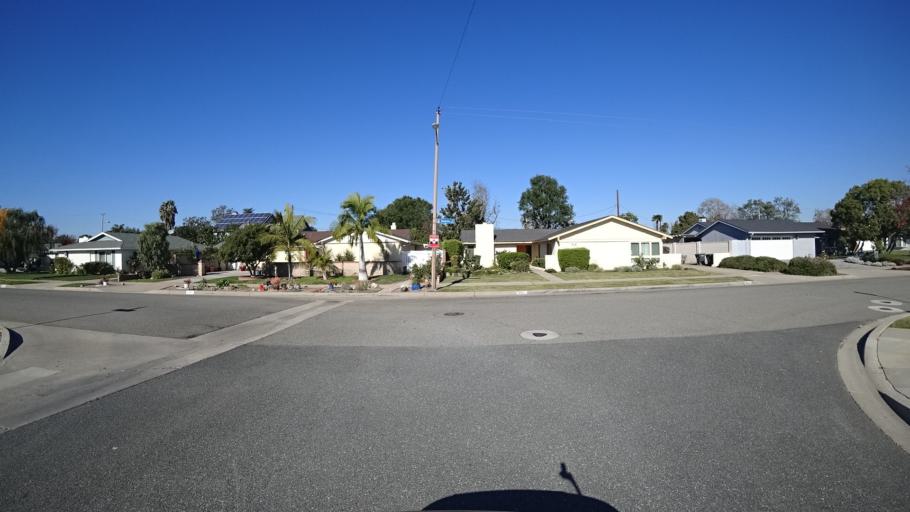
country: US
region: California
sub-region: Orange County
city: Tustin
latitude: 33.7741
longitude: -117.8216
